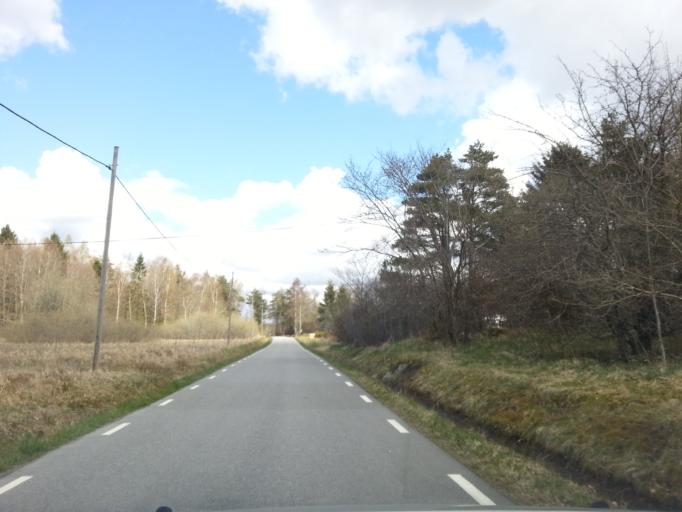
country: SE
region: Vaestra Goetaland
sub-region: Kungalvs Kommun
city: Kungalv
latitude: 57.8565
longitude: 11.9498
